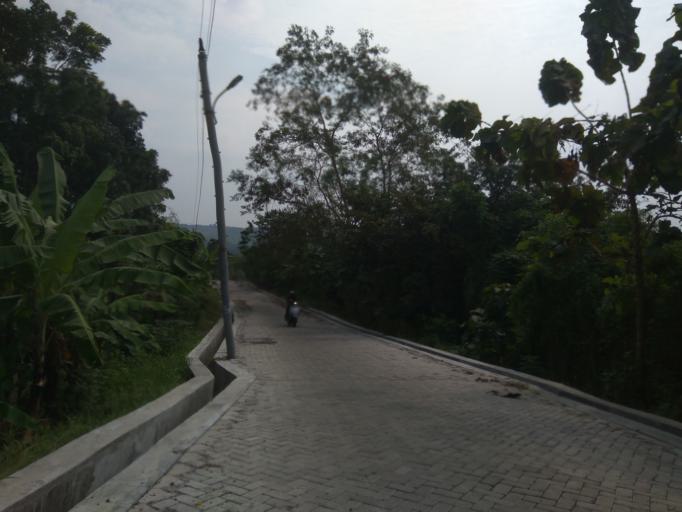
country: ID
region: Central Java
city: Semarang
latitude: -7.0354
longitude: 110.4130
